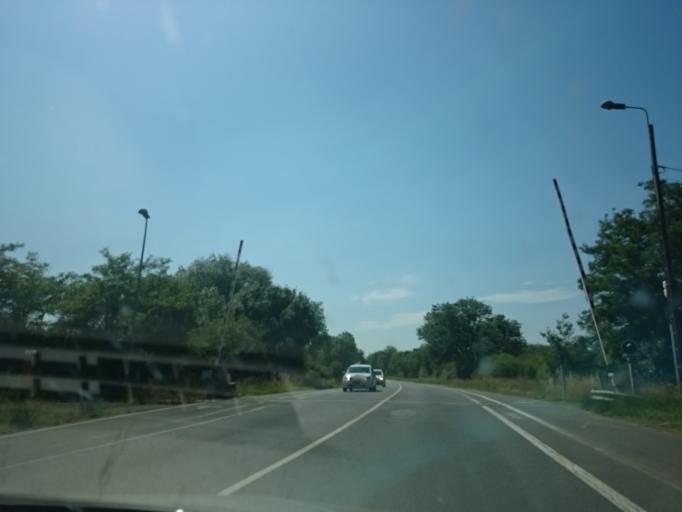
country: FR
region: Pays de la Loire
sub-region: Departement de la Loire-Atlantique
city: La Montagne
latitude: 47.2086
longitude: -1.6890
